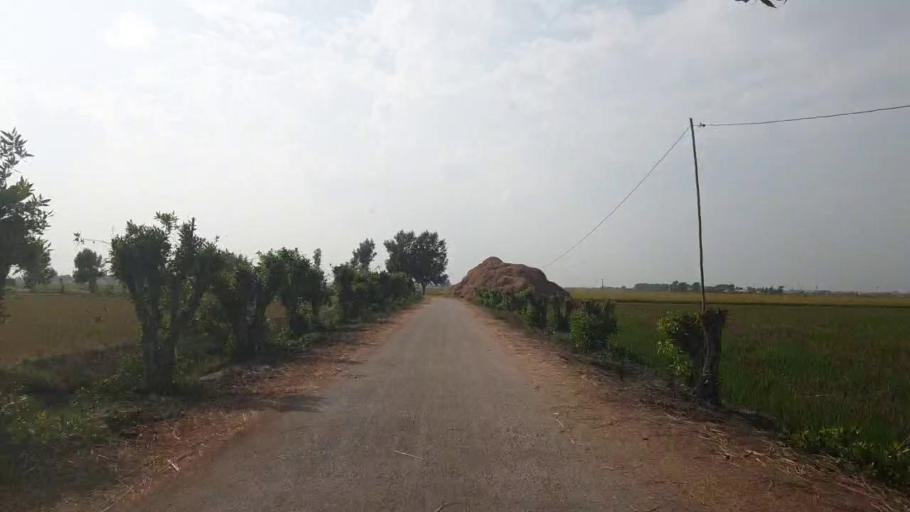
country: PK
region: Sindh
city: Kario
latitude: 24.6404
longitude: 68.5591
